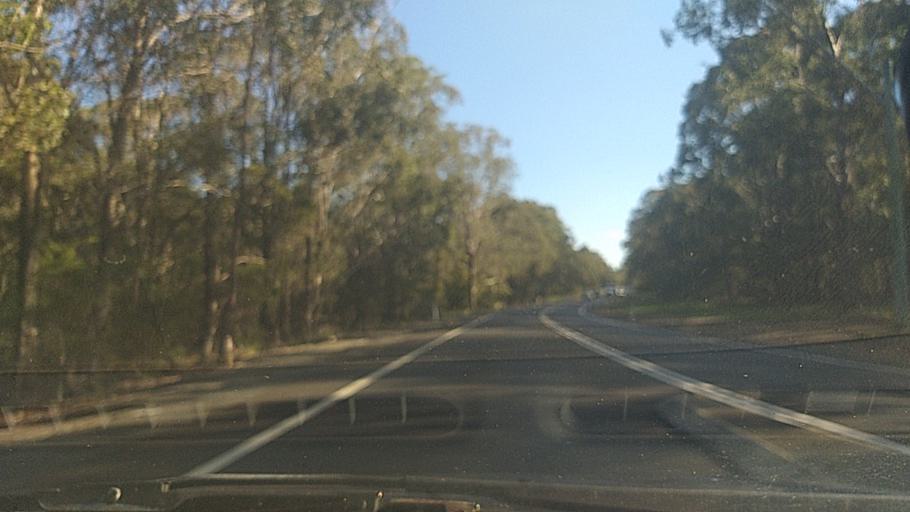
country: AU
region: New South Wales
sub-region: Penrith Municipality
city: Werrington Downs
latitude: -33.7058
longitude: 150.7239
